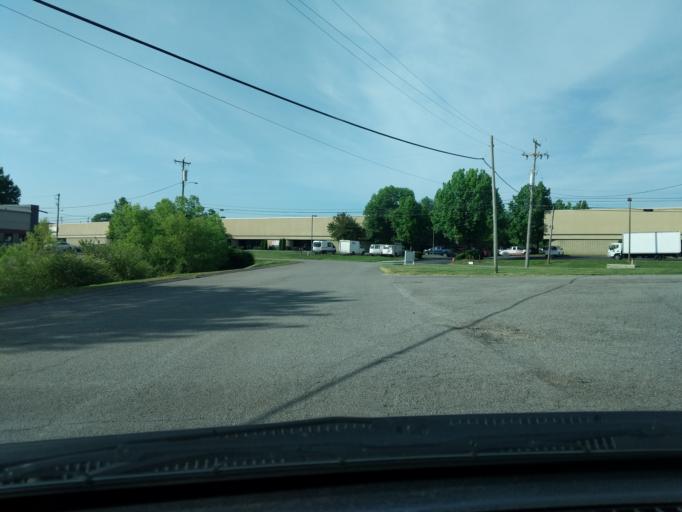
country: US
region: Tennessee
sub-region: Davidson County
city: Oak Hill
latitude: 36.0914
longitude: -86.6897
